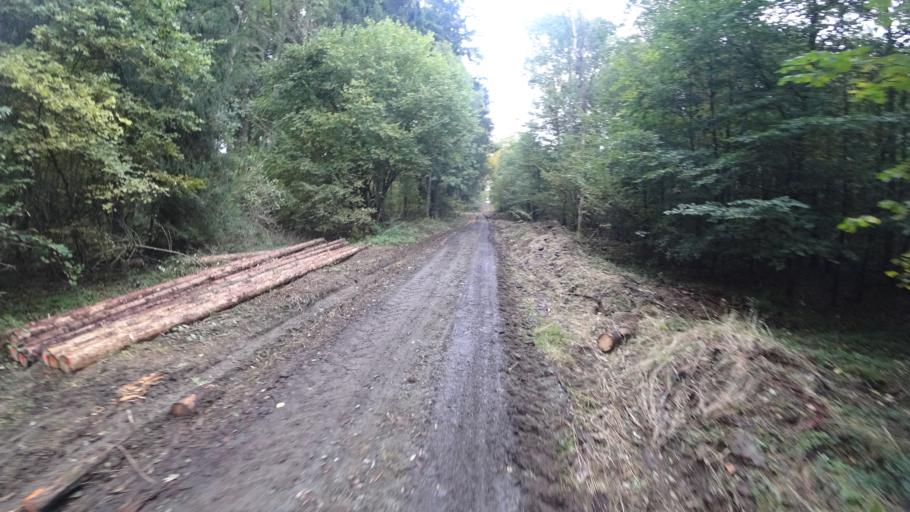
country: DE
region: Rheinland-Pfalz
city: Ruckeroth
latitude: 50.5587
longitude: 7.7664
